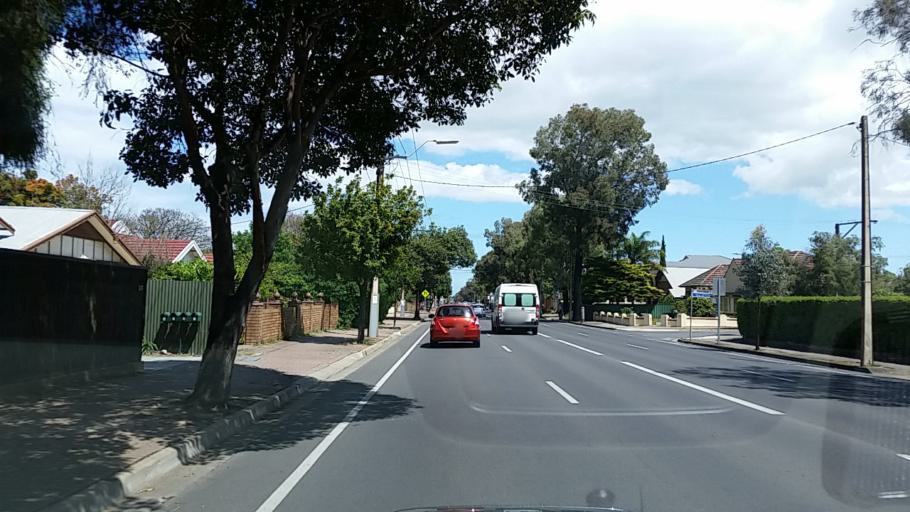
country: AU
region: South Australia
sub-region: Norwood Payneham St Peters
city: Trinity Gardens
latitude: -34.9145
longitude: 138.6480
